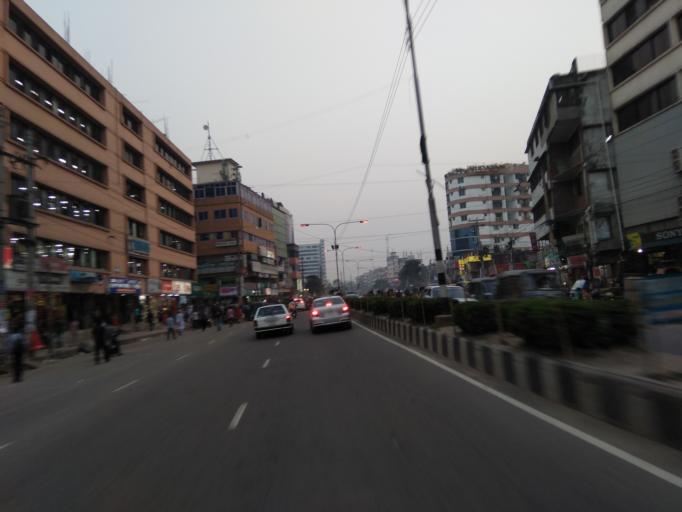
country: BD
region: Dhaka
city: Paltan
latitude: 23.7944
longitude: 90.3879
